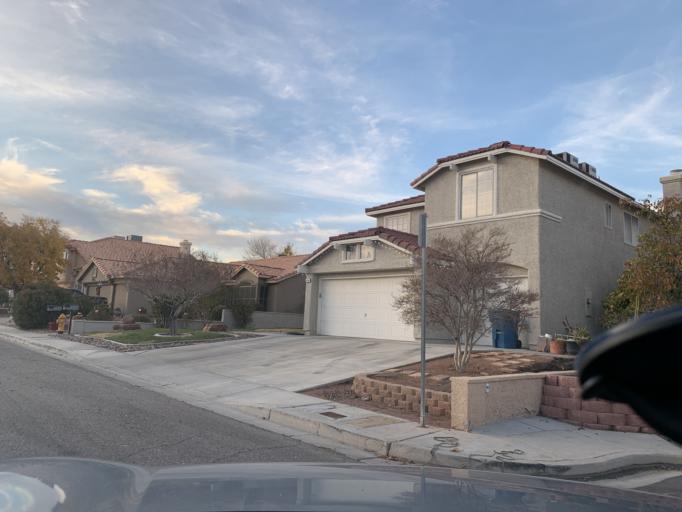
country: US
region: Nevada
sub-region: Clark County
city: Spring Valley
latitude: 36.0921
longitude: -115.2343
